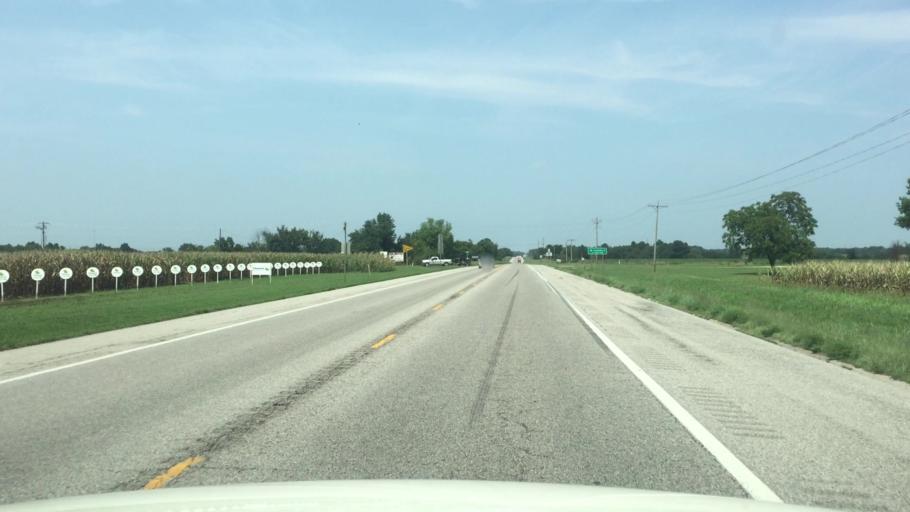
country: US
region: Kansas
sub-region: Crawford County
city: Pittsburg
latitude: 37.2791
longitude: -94.7053
